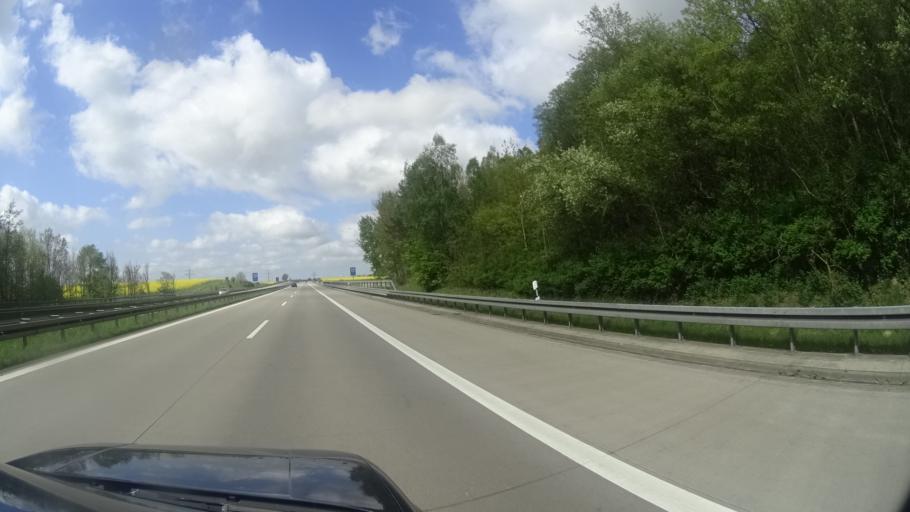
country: DE
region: Mecklenburg-Vorpommern
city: Kavelstorf
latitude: 53.9764
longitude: 12.1972
